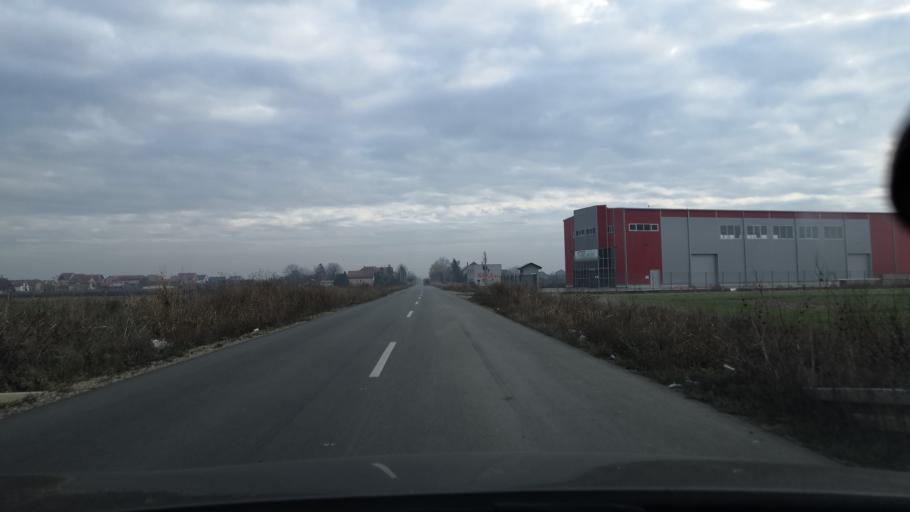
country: RS
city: Ugrinovci
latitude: 44.8803
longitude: 20.1640
